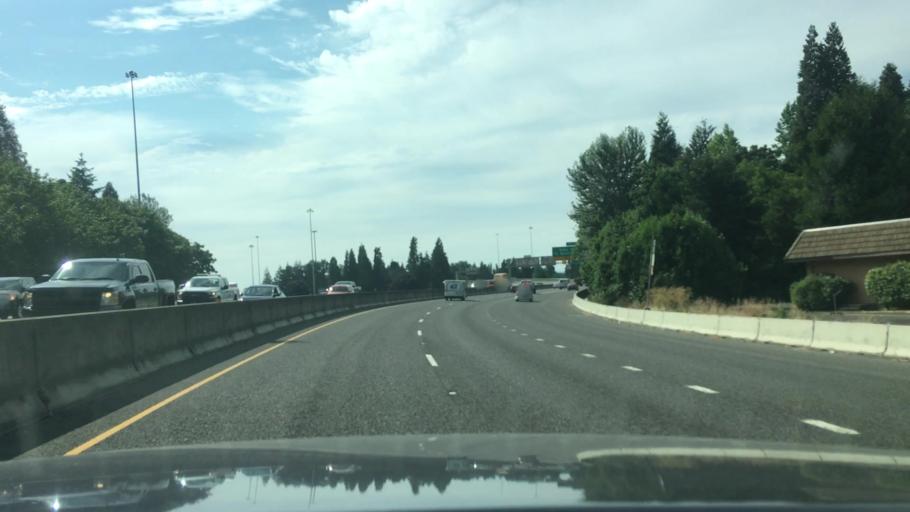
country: US
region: Oregon
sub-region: Lane County
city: Eugene
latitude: 44.0631
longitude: -123.0943
